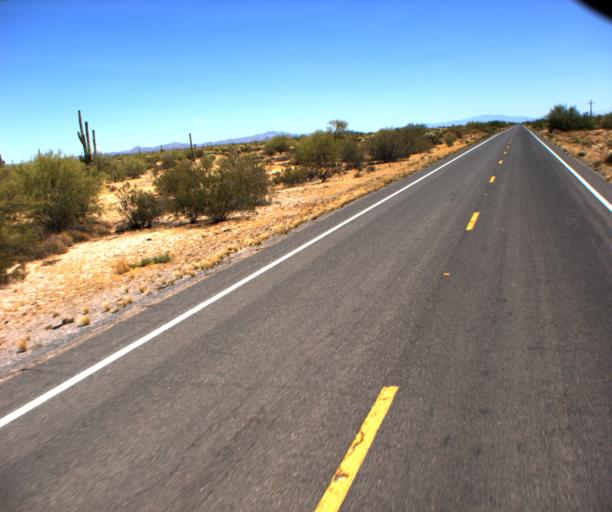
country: US
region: Arizona
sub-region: Pinal County
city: Florence
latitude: 32.9426
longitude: -111.3184
